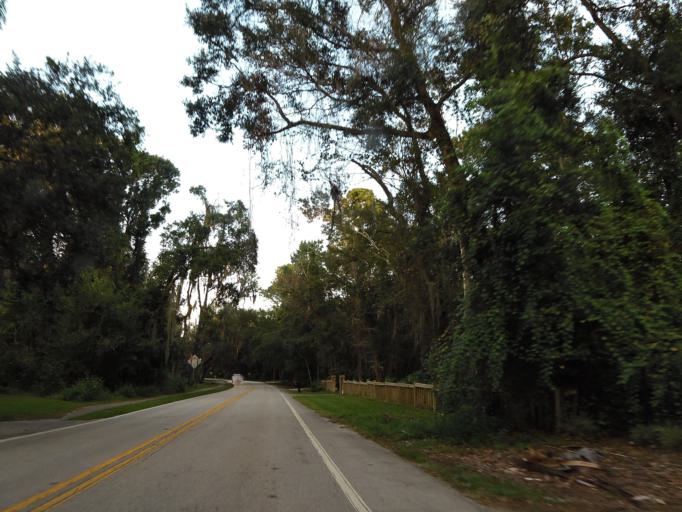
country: US
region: Florida
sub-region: Saint Johns County
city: Fruit Cove
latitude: 30.1861
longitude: -81.6332
